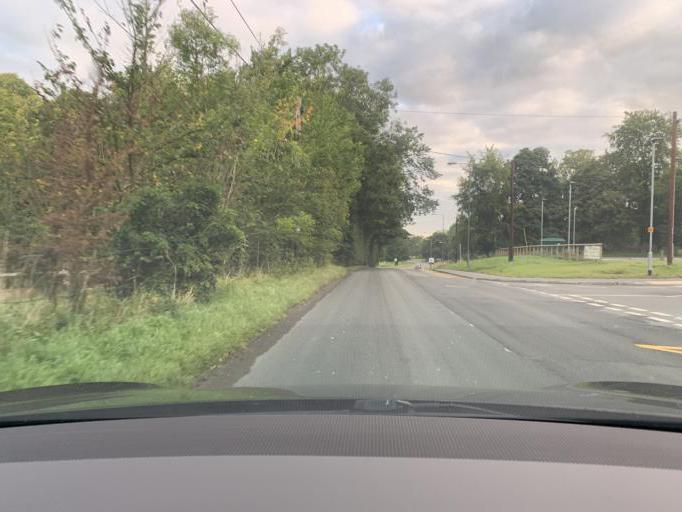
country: GB
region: England
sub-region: Wiltshire
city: Tidworth
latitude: 51.2296
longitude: -1.6639
